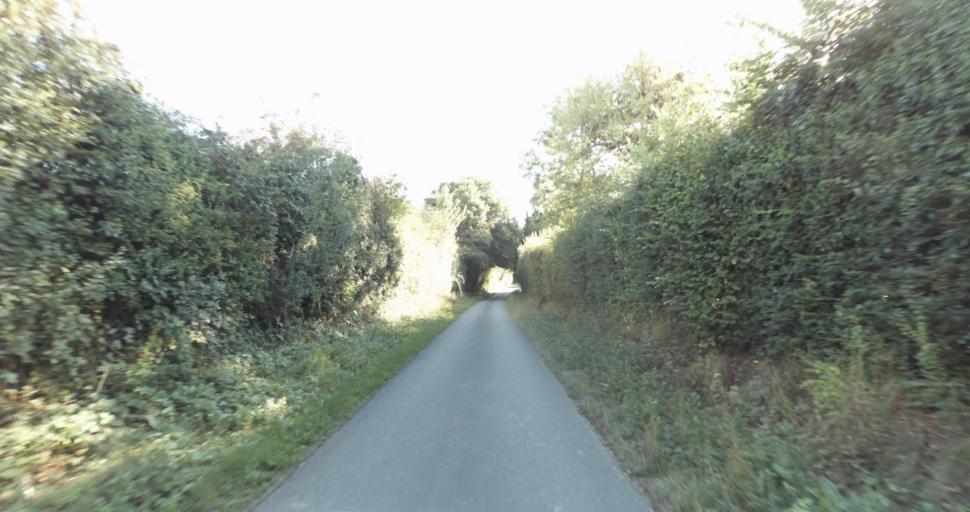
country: FR
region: Lower Normandy
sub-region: Departement de l'Orne
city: Vimoutiers
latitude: 48.8844
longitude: 0.1288
